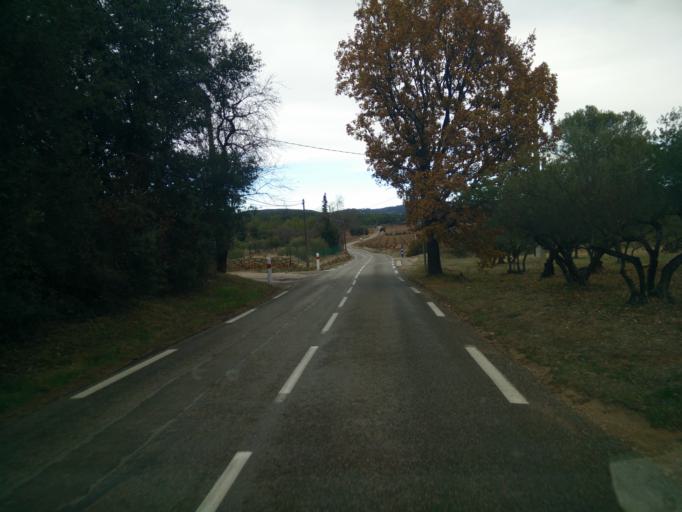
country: FR
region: Provence-Alpes-Cote d'Azur
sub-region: Departement du Var
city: Carces
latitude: 43.4803
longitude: 6.1363
